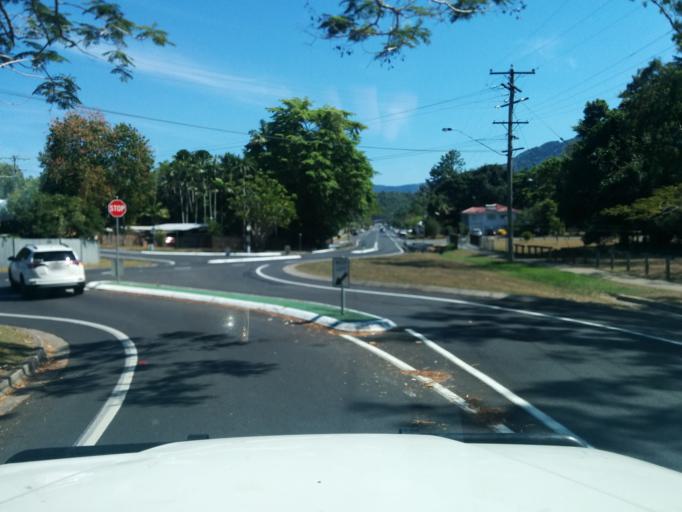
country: AU
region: Queensland
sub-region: Cairns
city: Redlynch
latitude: -16.9022
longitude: 145.7289
